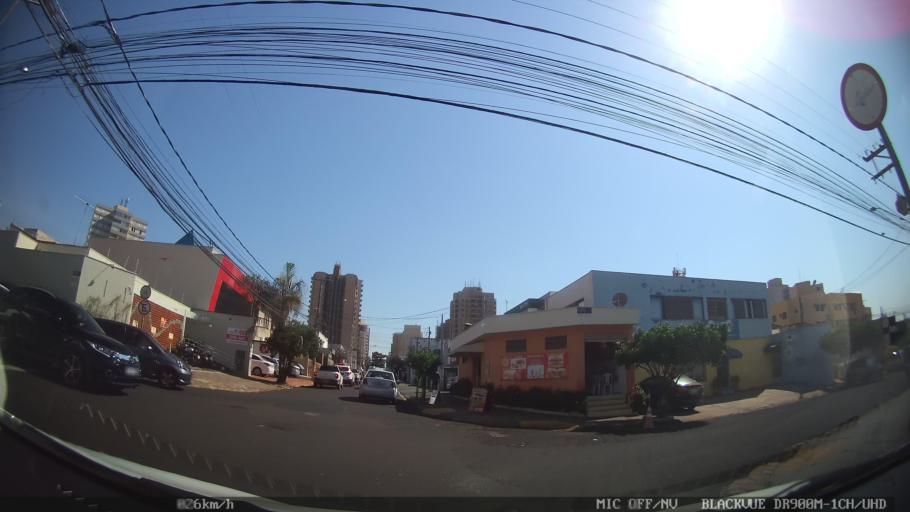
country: BR
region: Sao Paulo
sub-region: Ribeirao Preto
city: Ribeirao Preto
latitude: -21.1868
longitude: -47.8047
